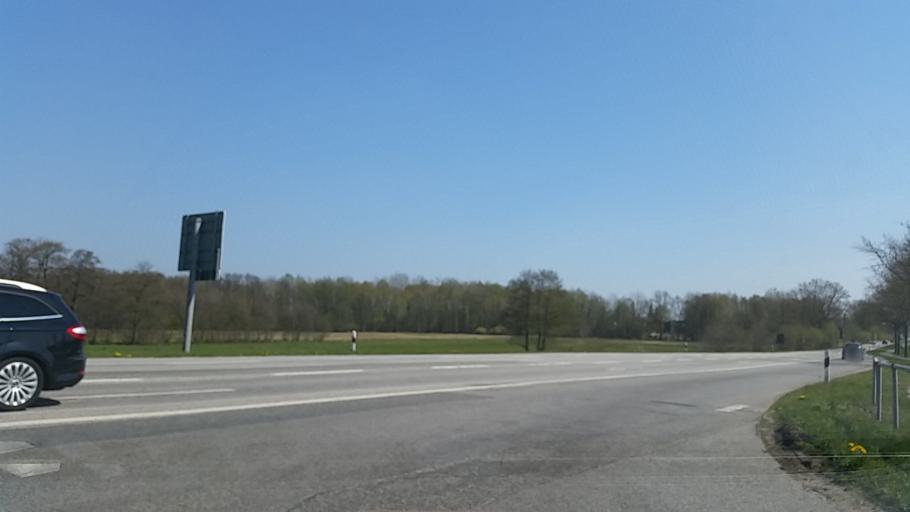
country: DE
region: Schleswig-Holstein
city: Bornsen
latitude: 53.4906
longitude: 10.2713
